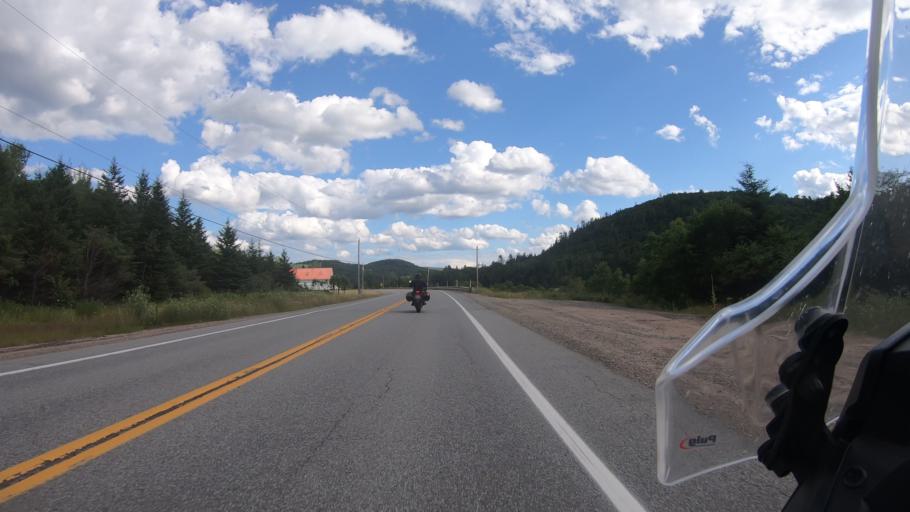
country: CA
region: Quebec
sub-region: Mauricie
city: Saint-Tite
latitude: 46.9871
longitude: -72.9112
